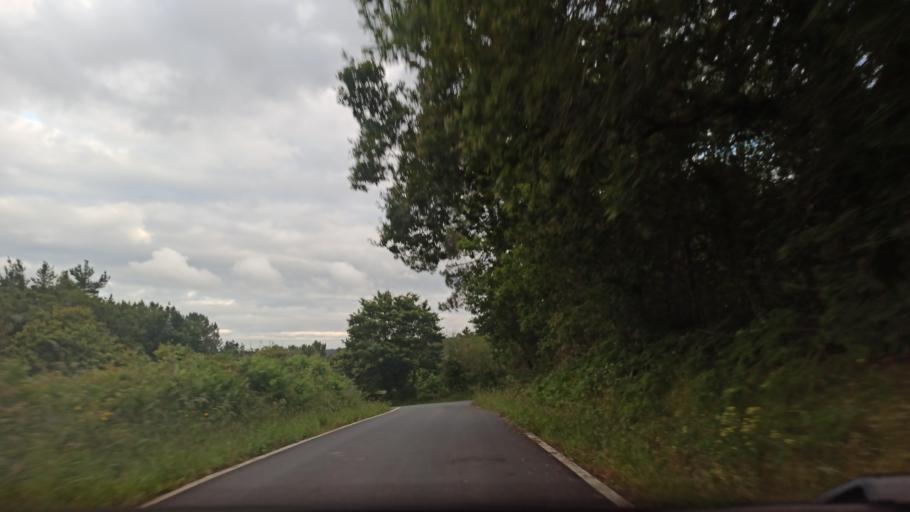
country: ES
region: Galicia
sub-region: Provincia da Coruna
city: Santiso
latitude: 42.8245
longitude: -8.1376
